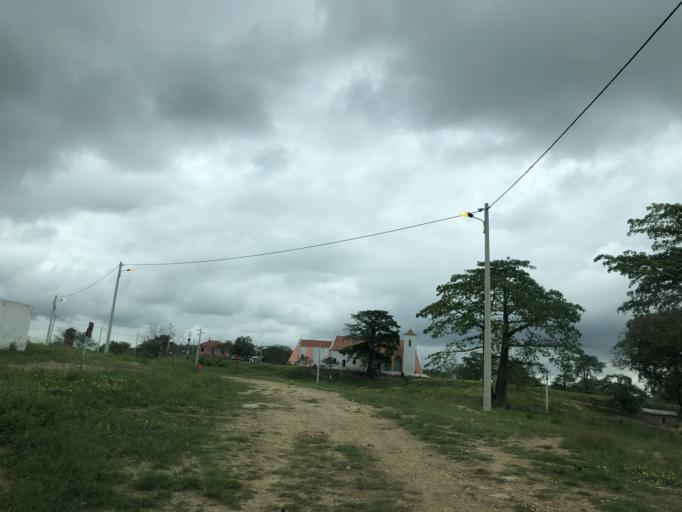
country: AO
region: Cuanza Norte
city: N'dalatando
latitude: -9.6292
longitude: 14.2568
